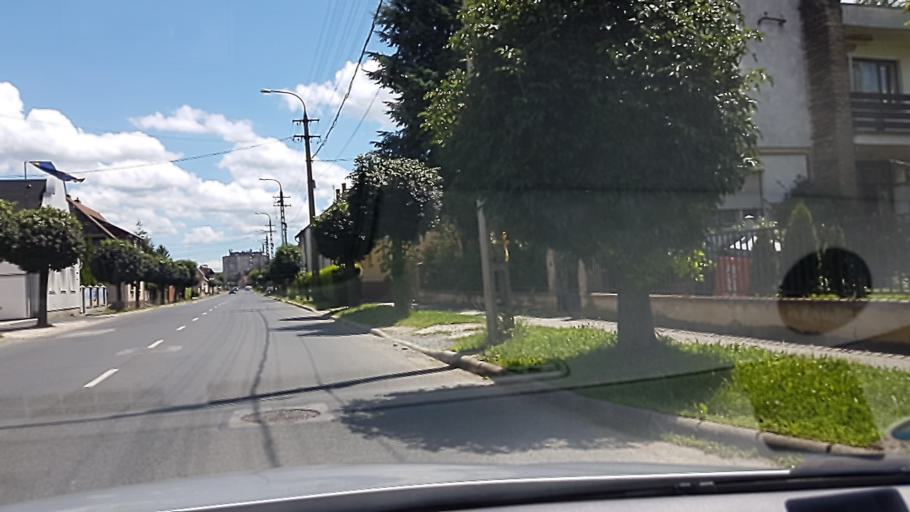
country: HU
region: Zala
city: Zalaegerszeg
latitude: 46.8503
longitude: 16.8196
